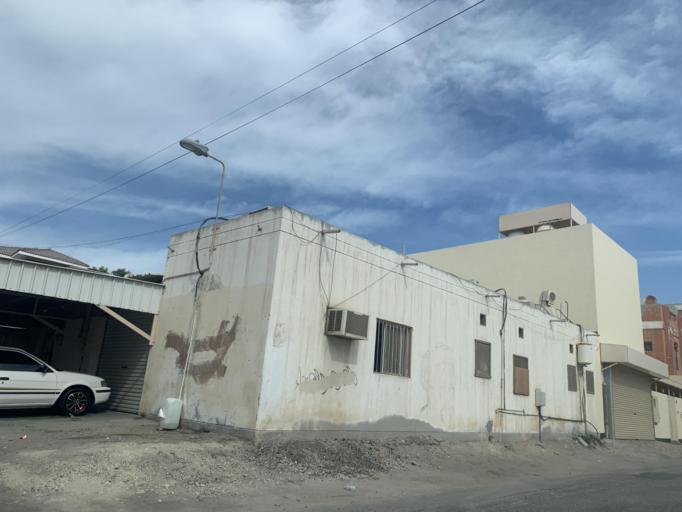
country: BH
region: Central Governorate
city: Madinat Hamad
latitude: 26.1212
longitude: 50.4796
